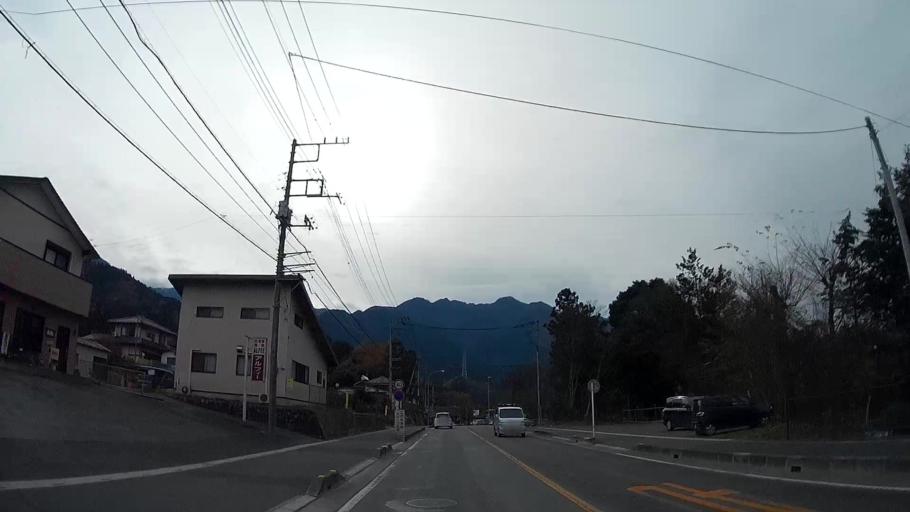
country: JP
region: Saitama
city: Chichibu
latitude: 35.9548
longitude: 139.0282
